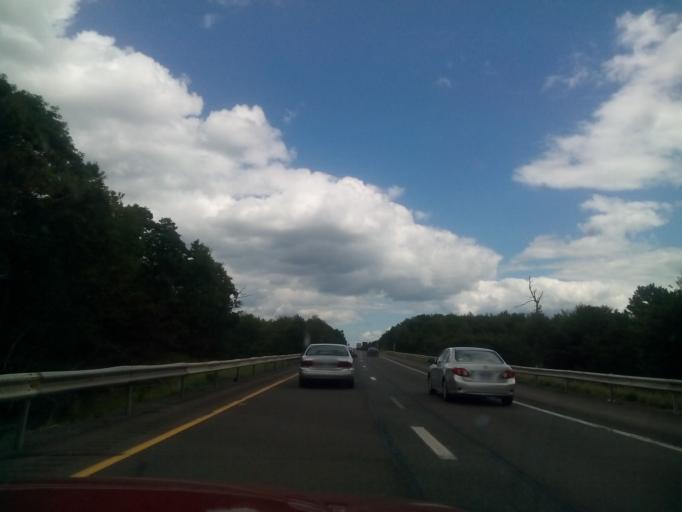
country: US
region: Pennsylvania
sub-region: Monroe County
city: Emerald Lakes
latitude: 41.0714
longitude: -75.4157
